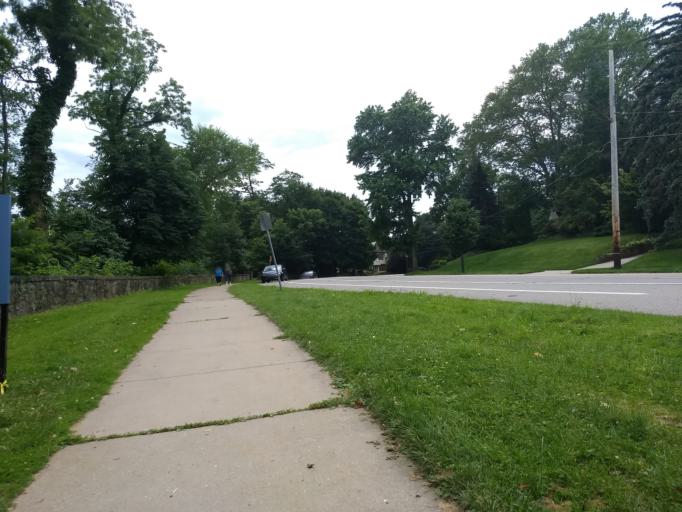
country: US
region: Pennsylvania
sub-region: Allegheny County
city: Wilkinsburg
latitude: 40.4363
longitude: -79.9087
